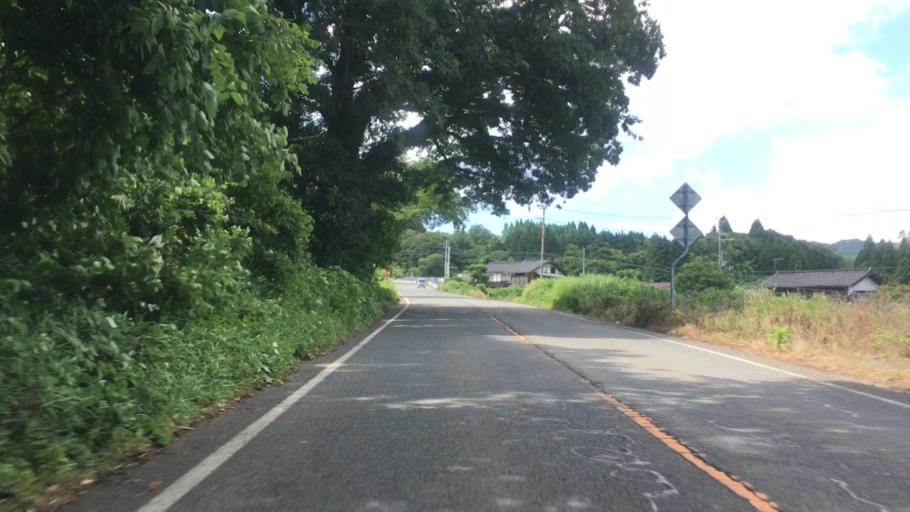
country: JP
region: Hyogo
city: Toyooka
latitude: 35.4875
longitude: 134.6917
